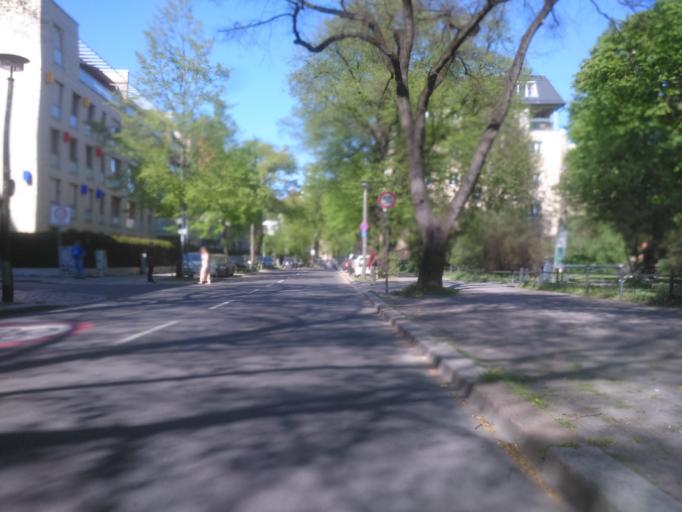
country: DE
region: Berlin
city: Weissensee
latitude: 52.5555
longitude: 13.4586
